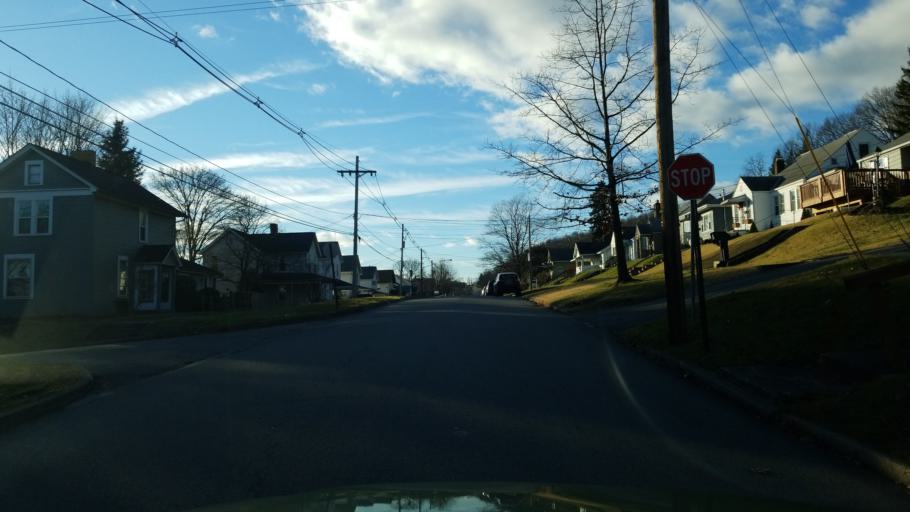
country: US
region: Pennsylvania
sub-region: Indiana County
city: Indiana
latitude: 40.6245
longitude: -79.1656
